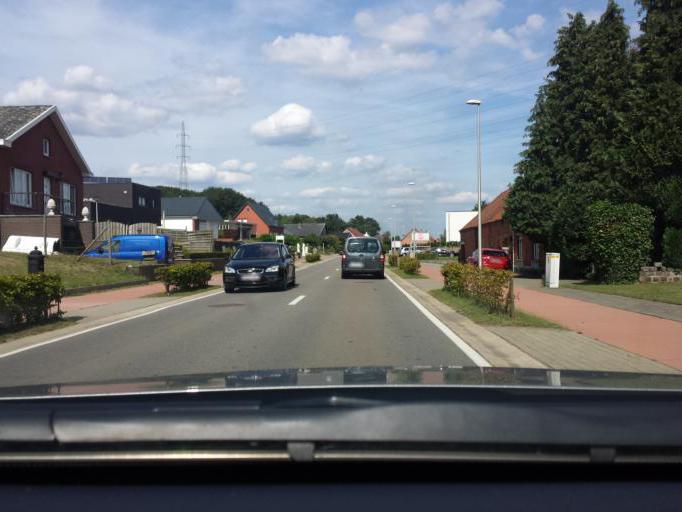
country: BE
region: Flanders
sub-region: Provincie Limburg
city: Lummen
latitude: 50.9938
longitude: 5.2304
